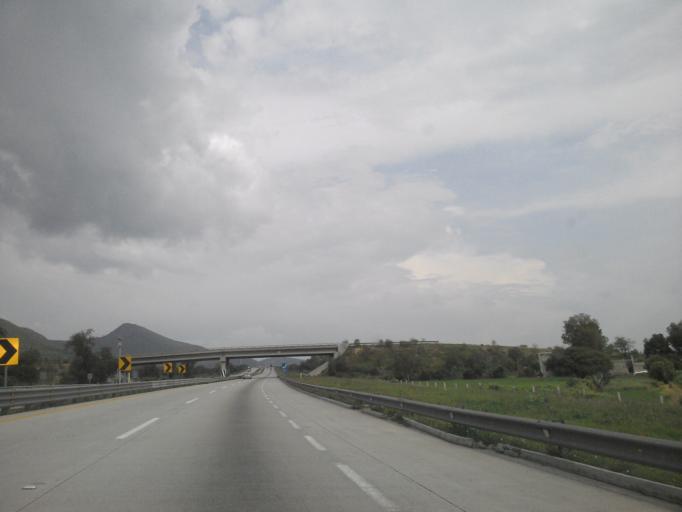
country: MX
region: Hidalgo
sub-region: Atitalaquia
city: Tezoquipa
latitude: 20.0579
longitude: -99.1940
